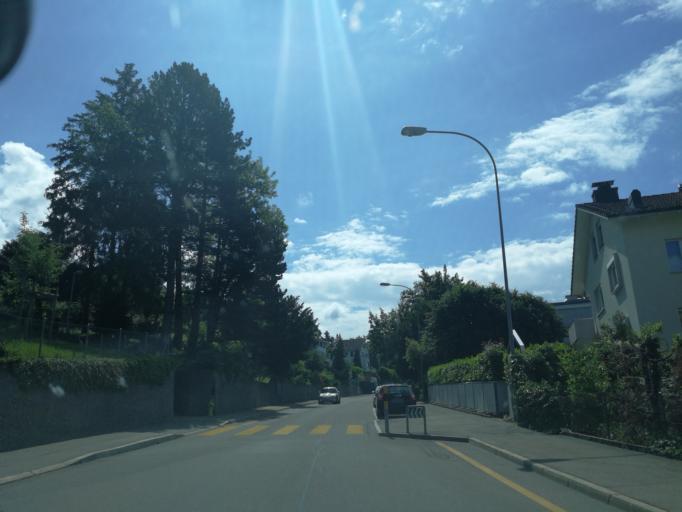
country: CH
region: Zurich
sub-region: Bezirk Meilen
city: Erlenbach
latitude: 47.3076
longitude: 8.5943
